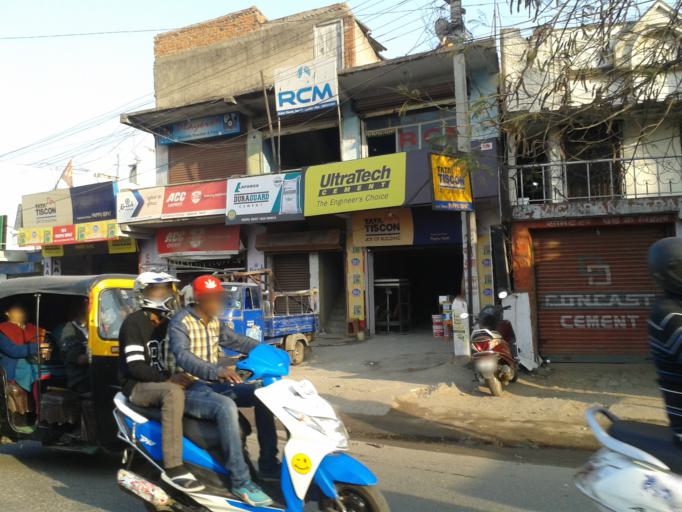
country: IN
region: Jharkhand
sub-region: Ranchi
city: Ranchi
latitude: 23.3774
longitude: 85.3602
